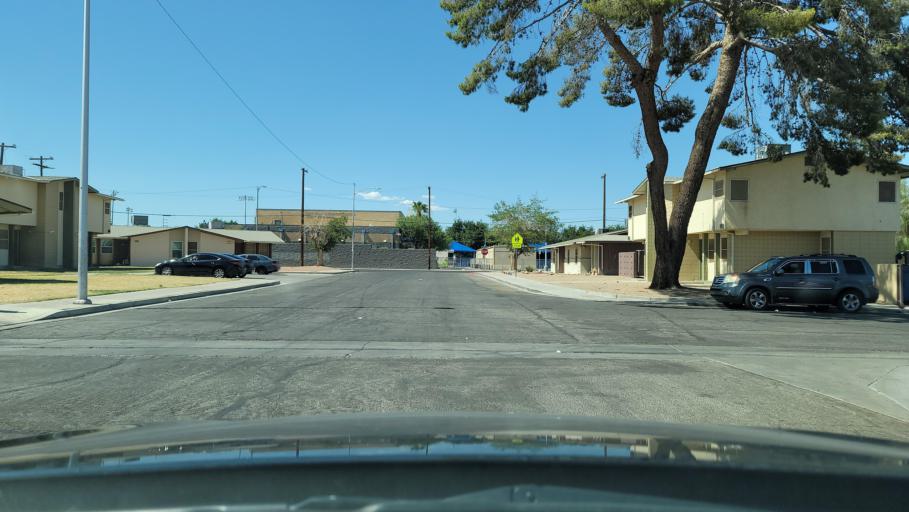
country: US
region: Nevada
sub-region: Clark County
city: Las Vegas
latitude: 36.1913
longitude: -115.1544
